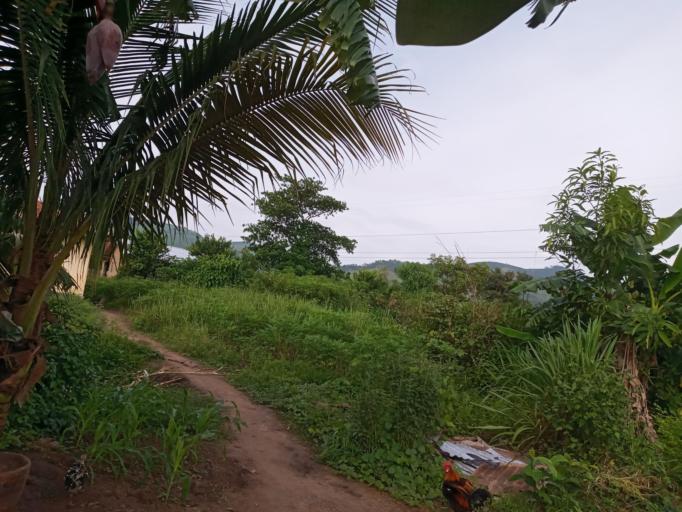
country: SL
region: Northern Province
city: Bumbuna
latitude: 9.0473
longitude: -11.7559
